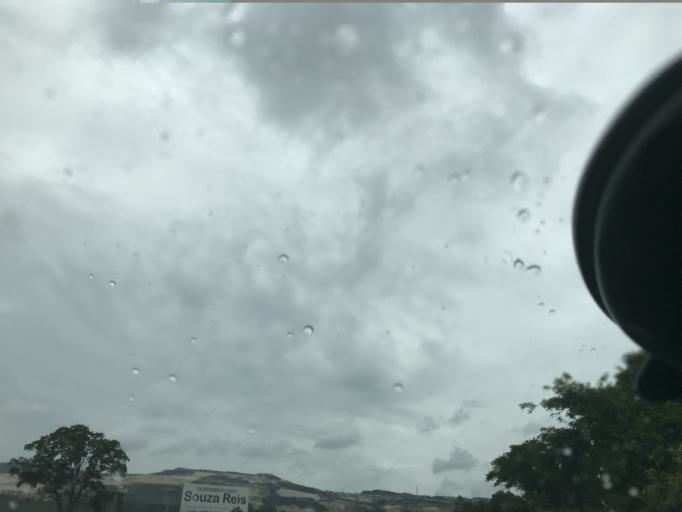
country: BR
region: Minas Gerais
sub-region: Conceicao Do Rio Verde
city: Conceicao do Rio Verde
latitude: -21.6960
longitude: -45.0017
